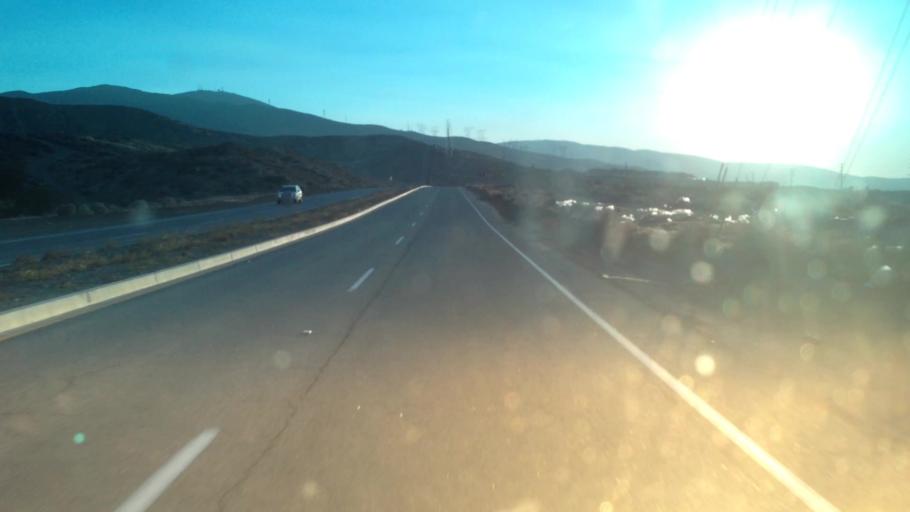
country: US
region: California
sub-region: Los Angeles County
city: Desert View Highlands
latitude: 34.5582
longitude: -118.1584
